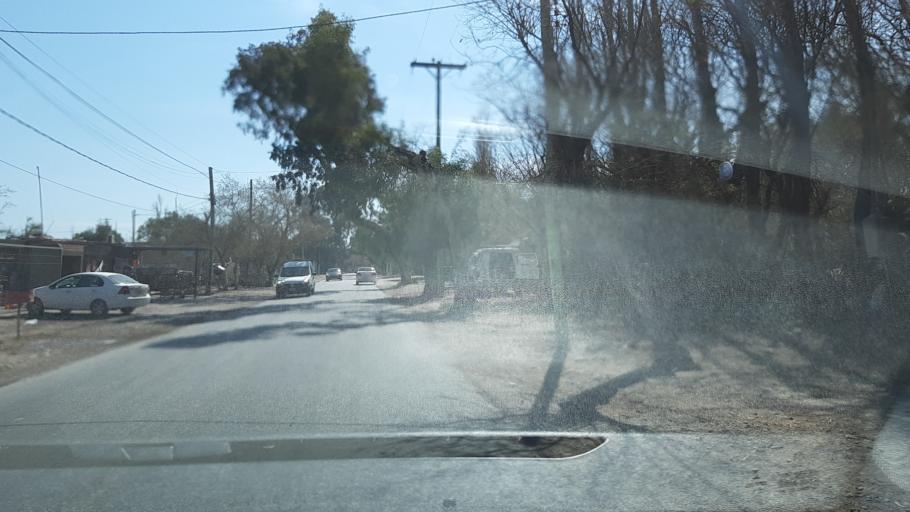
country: AR
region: San Juan
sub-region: Departamento de Rivadavia
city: Rivadavia
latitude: -31.5383
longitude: -68.6165
